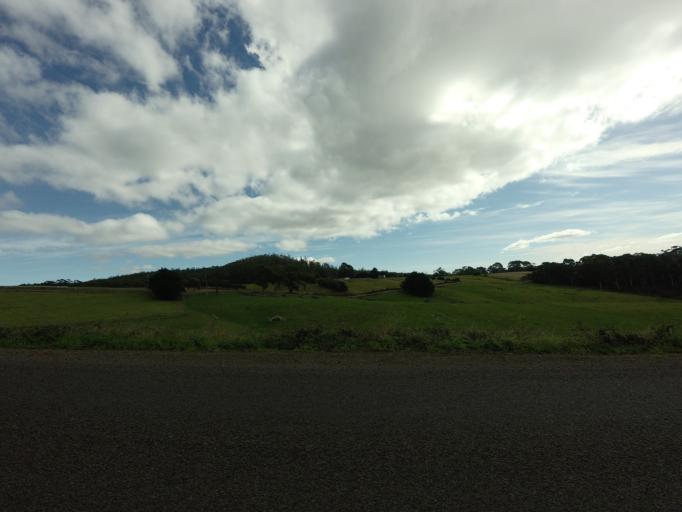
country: AU
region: Tasmania
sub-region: Clarence
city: Sandford
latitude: -43.0661
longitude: 147.7470
